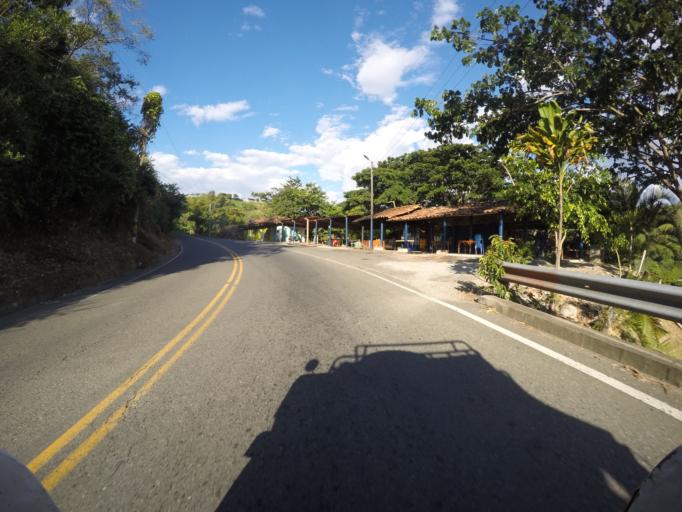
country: CO
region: Valle del Cauca
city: Alcala
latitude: 4.7041
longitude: -75.8388
